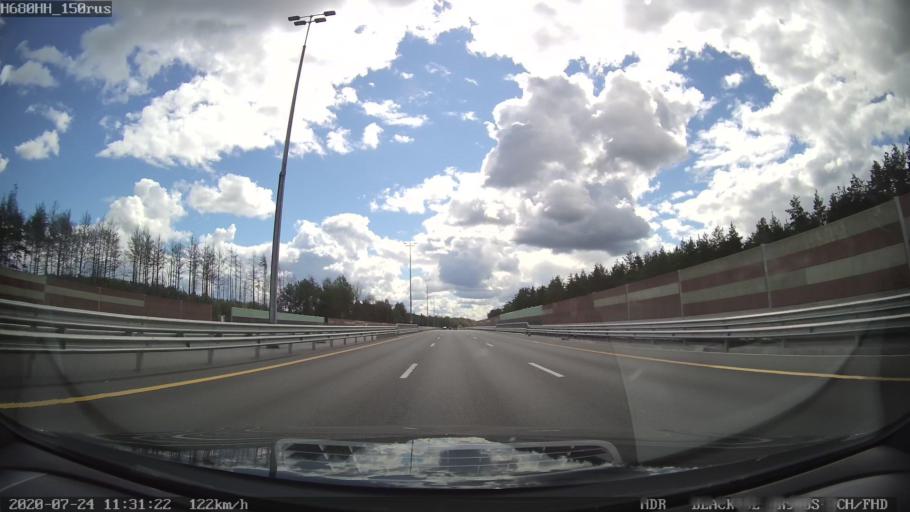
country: RU
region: Leningrad
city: Krasnyy Bor
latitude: 59.6574
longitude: 30.6358
